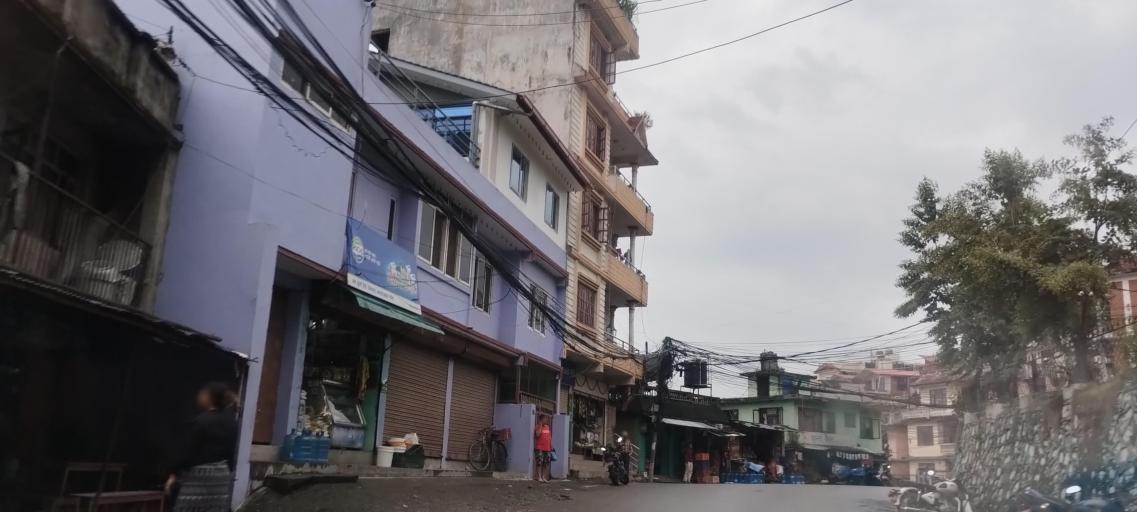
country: NP
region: Central Region
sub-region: Bagmati Zone
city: Kathmandu
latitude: 27.7092
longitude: 85.3400
